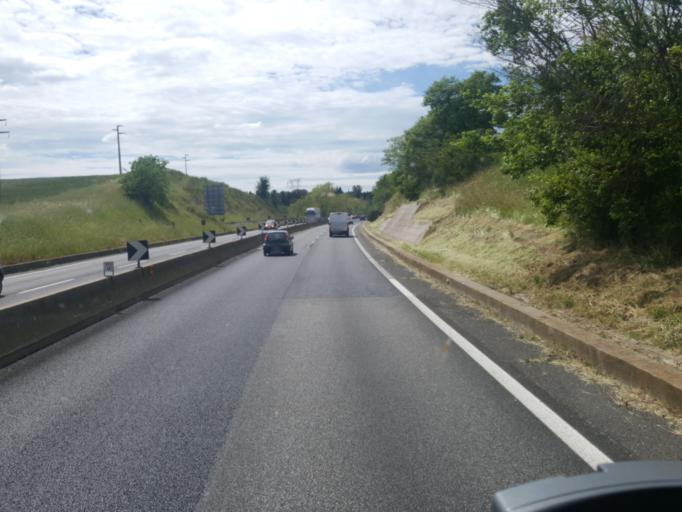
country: IT
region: Latium
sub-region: Citta metropolitana di Roma Capitale
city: La Massimina-Casal Lumbroso
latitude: 41.8856
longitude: 12.3223
